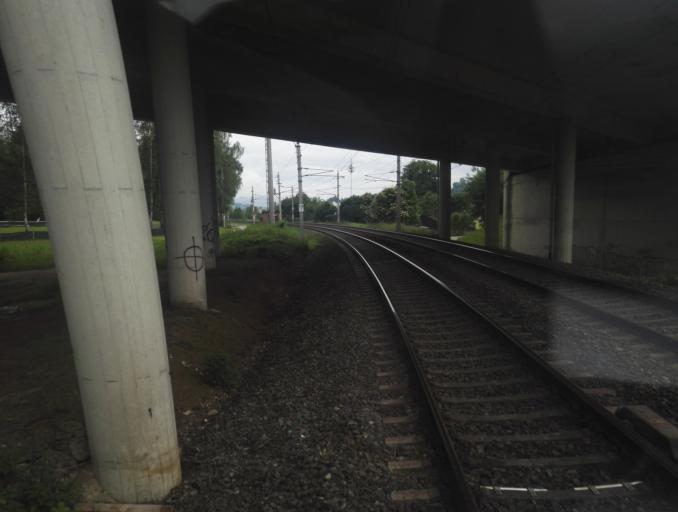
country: AT
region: Styria
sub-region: Politischer Bezirk Bruck-Muerzzuschlag
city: Kindberg
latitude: 47.5110
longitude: 15.4601
